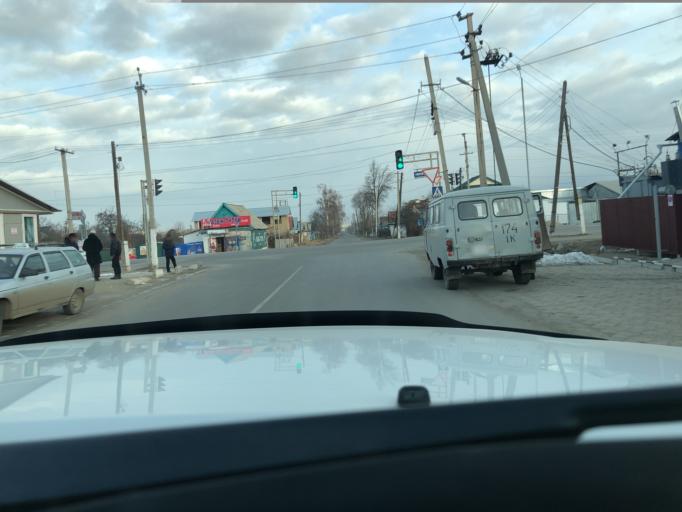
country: KG
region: Ysyk-Koel
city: Karakol
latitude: 42.4828
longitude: 78.3704
